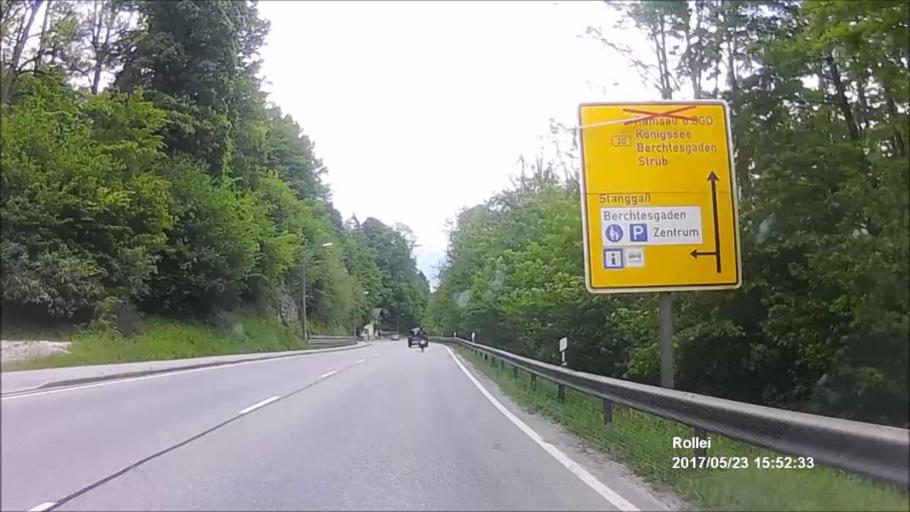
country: DE
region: Bavaria
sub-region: Upper Bavaria
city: Bischofswiesen
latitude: 47.6445
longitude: 12.9709
